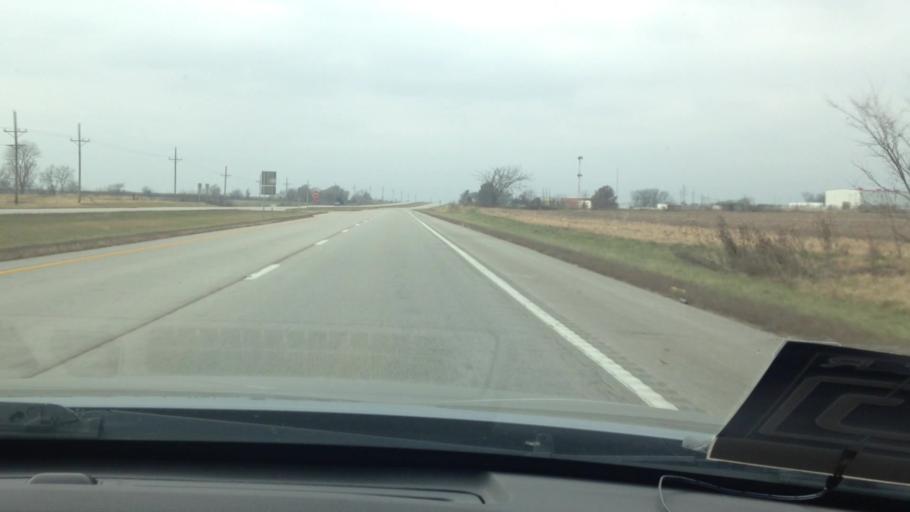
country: US
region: Missouri
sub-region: Cass County
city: Garden City
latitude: 38.5820
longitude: -94.2182
